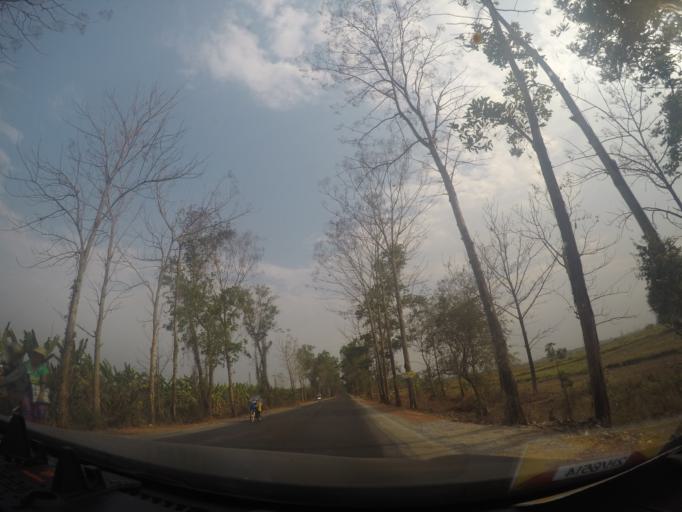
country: MM
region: Bago
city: Paungde
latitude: 18.2746
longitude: 95.6391
